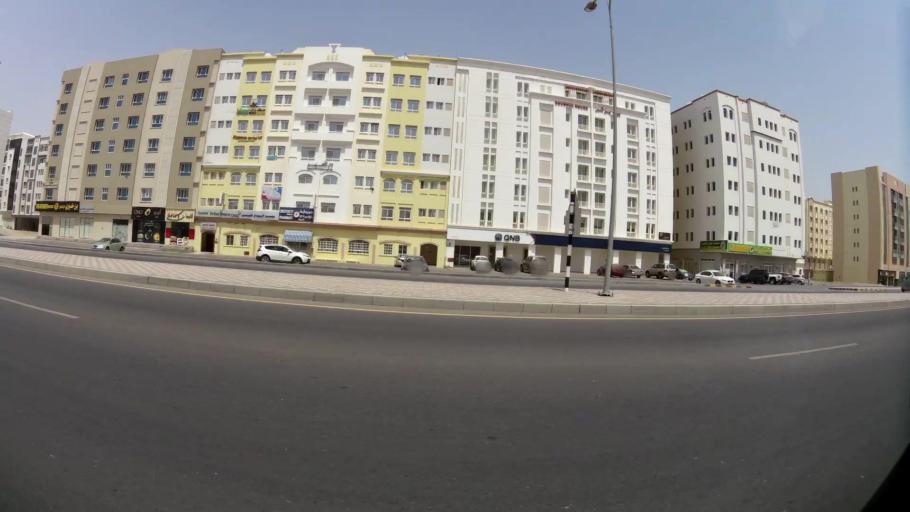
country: OM
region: Muhafazat Masqat
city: Bawshar
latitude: 23.5598
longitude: 58.4020
